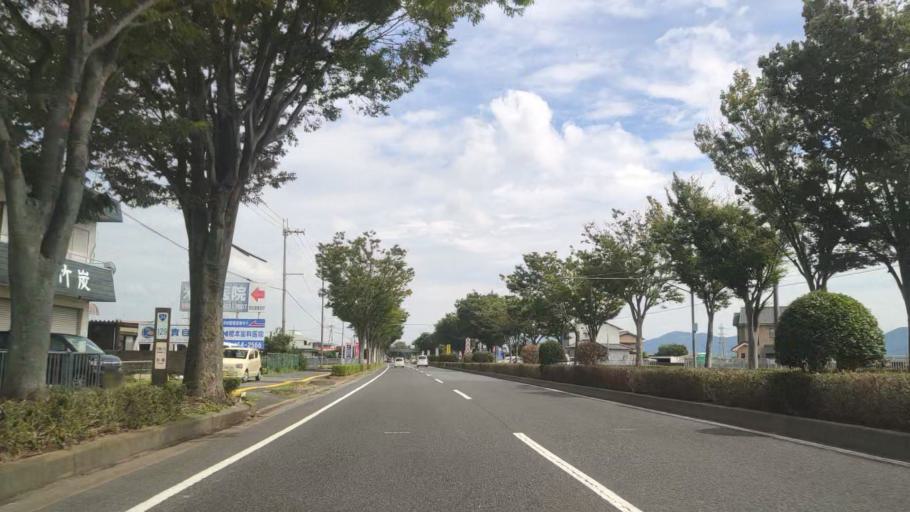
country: JP
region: Wakayama
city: Iwade
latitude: 34.2548
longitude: 135.2497
